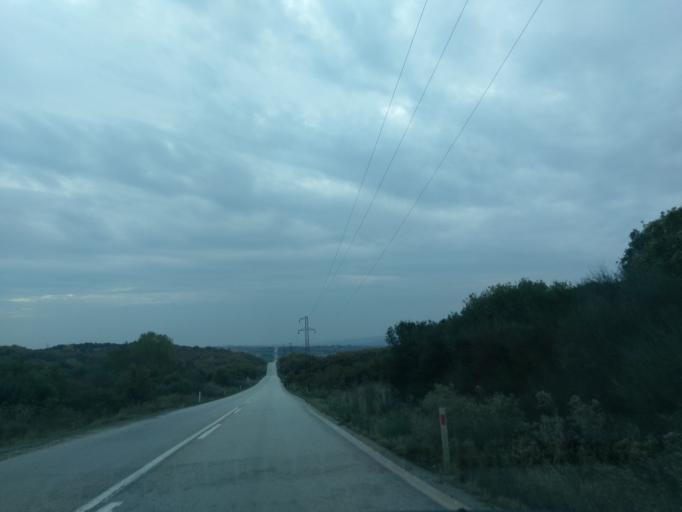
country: TR
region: Istanbul
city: Canta
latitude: 41.1590
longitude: 28.1068
